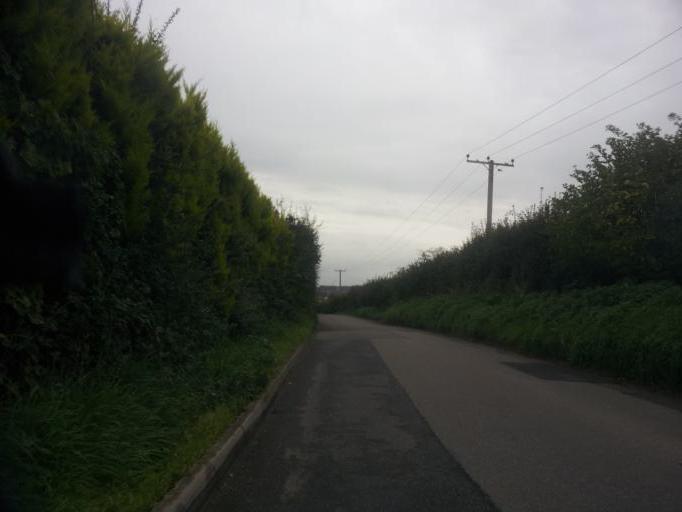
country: GB
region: England
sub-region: Kent
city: Teynham
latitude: 51.3299
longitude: 0.7697
